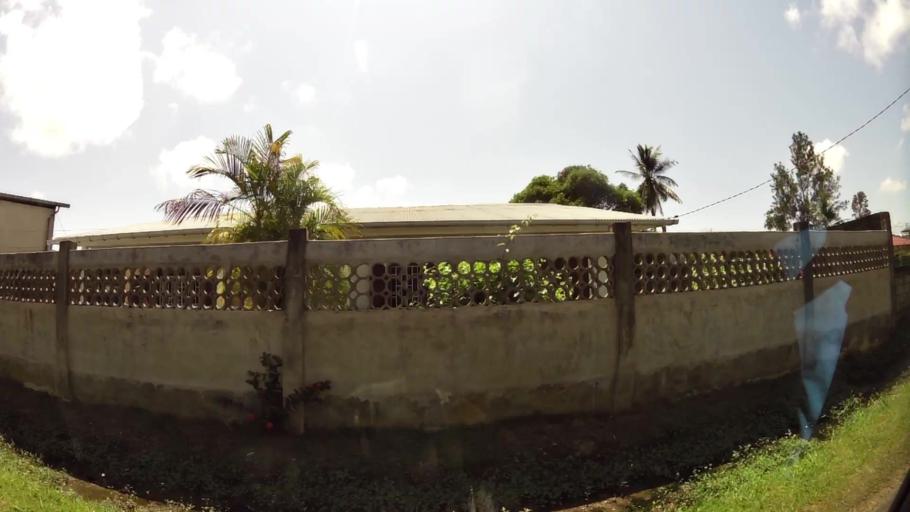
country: GF
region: Guyane
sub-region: Guyane
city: Cayenne
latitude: 4.9171
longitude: -52.3164
